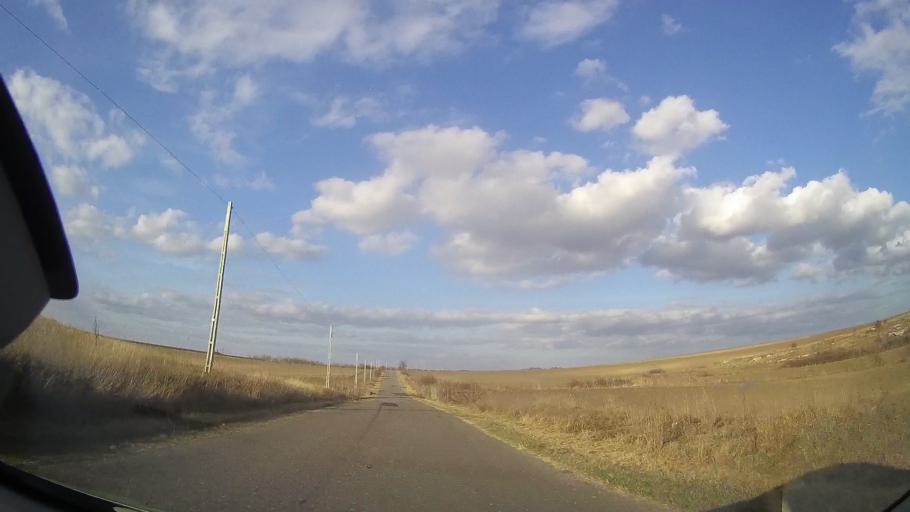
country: RO
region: Constanta
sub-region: Comuna Cerchezu
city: Cerchezu
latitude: 43.8426
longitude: 28.0984
